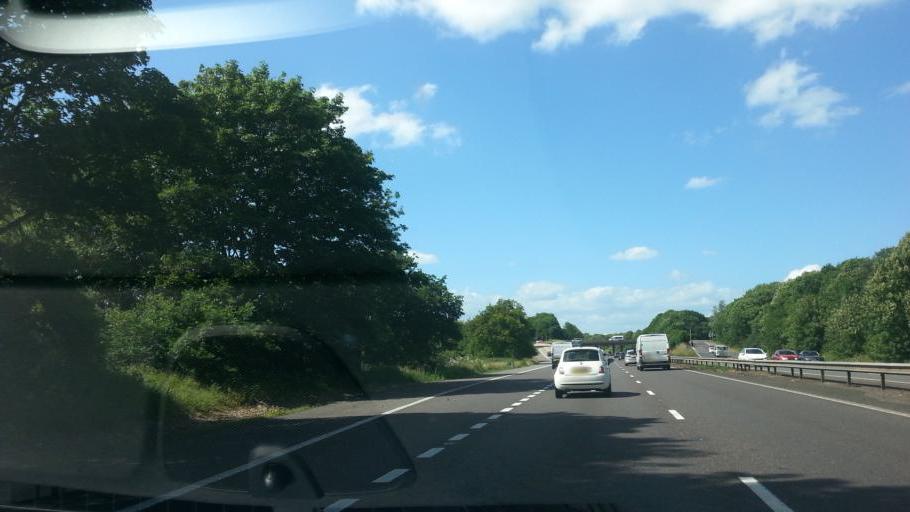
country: GB
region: England
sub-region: Hertfordshire
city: Stevenage
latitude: 51.8839
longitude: -0.2048
